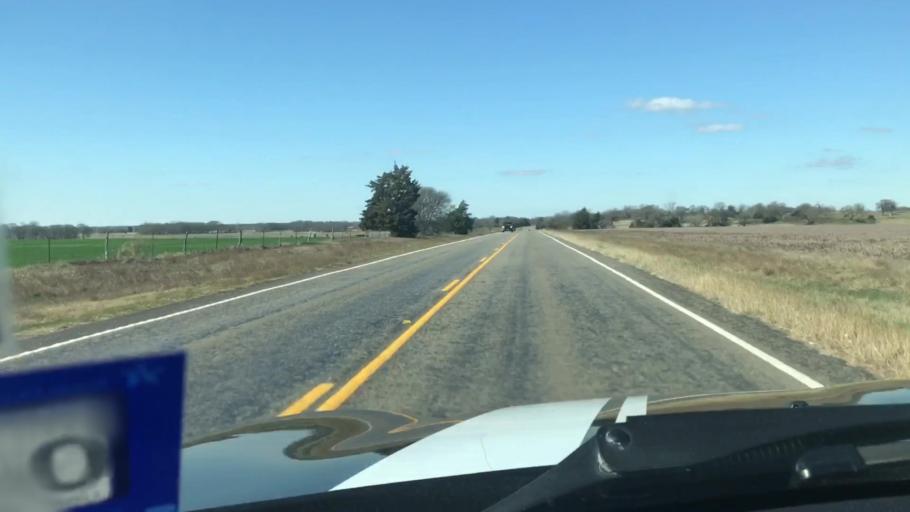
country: US
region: Texas
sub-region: Robertson County
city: Calvert
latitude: 30.8745
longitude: -96.7234
